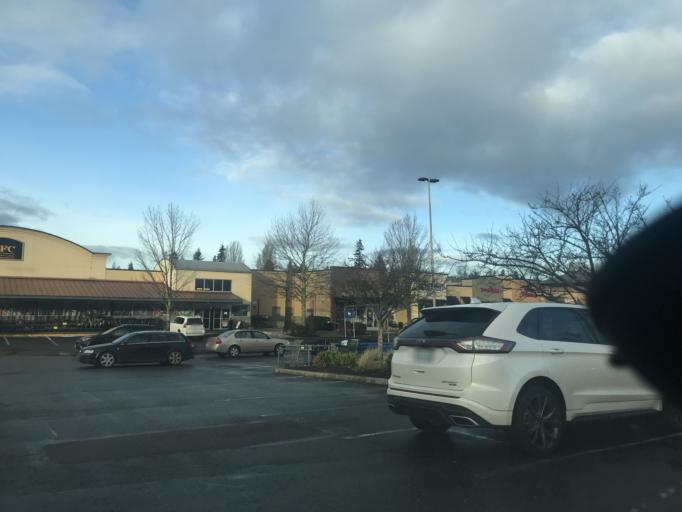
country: US
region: Washington
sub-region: King County
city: White Center
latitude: 47.5221
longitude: -122.3649
